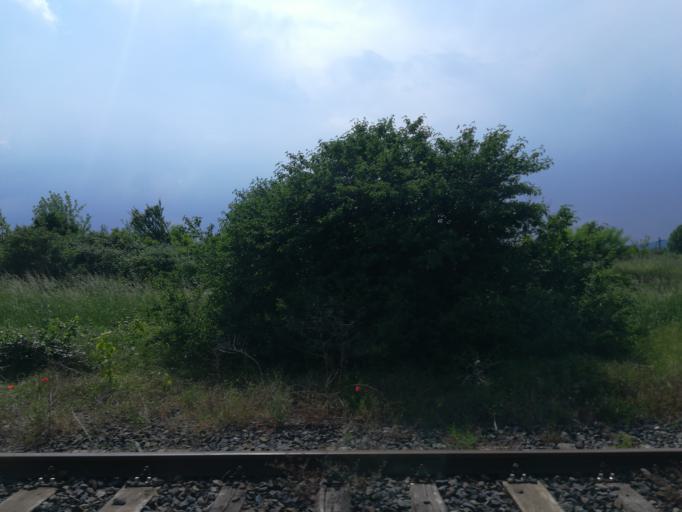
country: IT
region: Veneto
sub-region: Provincia di Vicenza
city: Dueville
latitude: 45.6376
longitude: 11.5436
